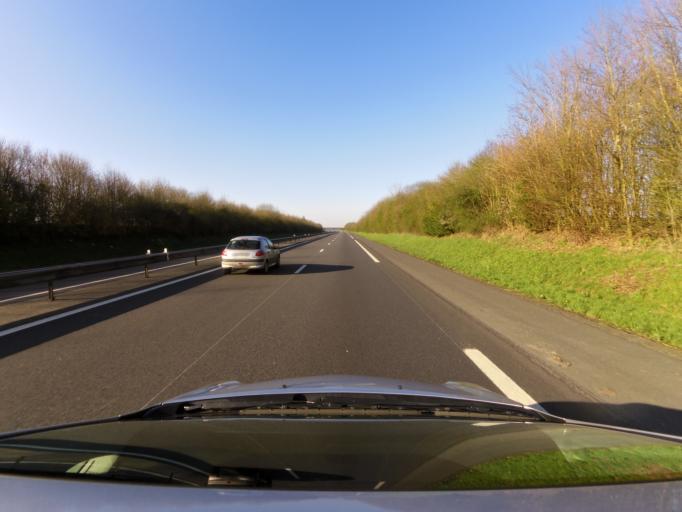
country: FR
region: Lower Normandy
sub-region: Departement du Calvados
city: Saint-Martin-des-Besaces
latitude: 49.0050
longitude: -0.9049
